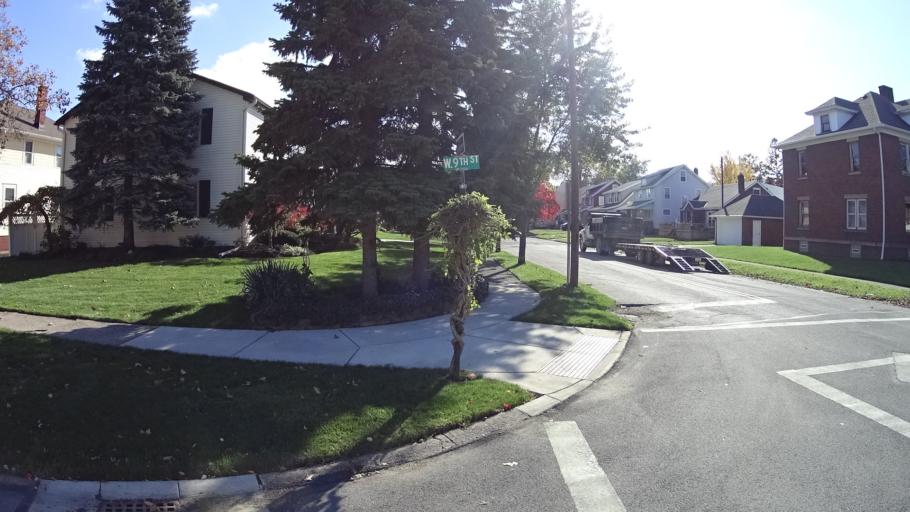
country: US
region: Ohio
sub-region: Lorain County
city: Lorain
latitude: 41.4606
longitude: -82.1908
